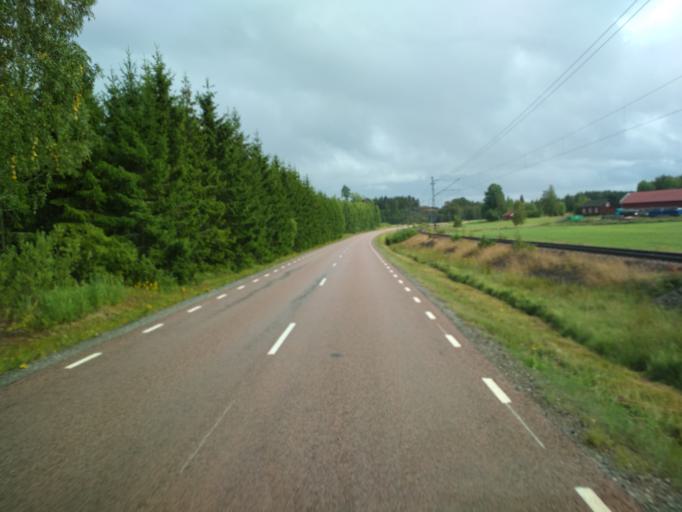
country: SE
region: Vaestmanland
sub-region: Surahammars Kommun
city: Ramnas
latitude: 59.8150
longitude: 16.1604
